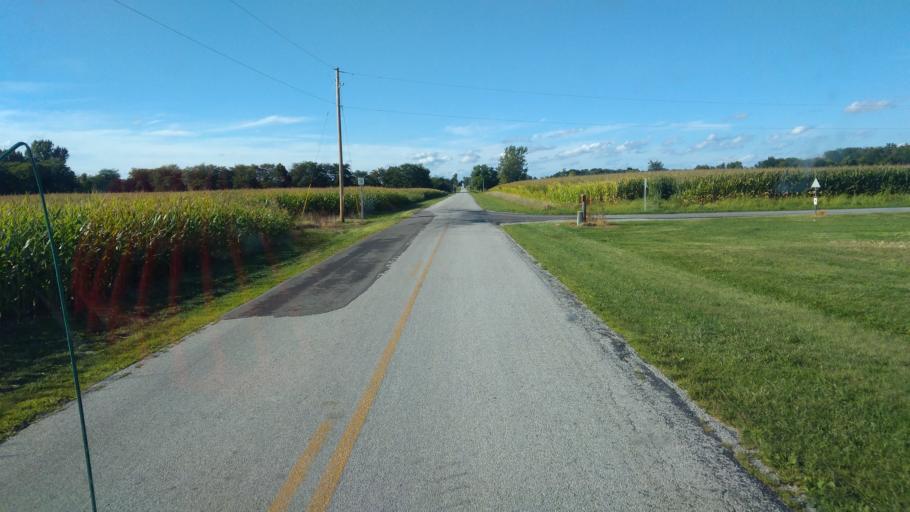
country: US
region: Ohio
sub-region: Hardin County
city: Forest
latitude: 40.7596
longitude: -83.5763
